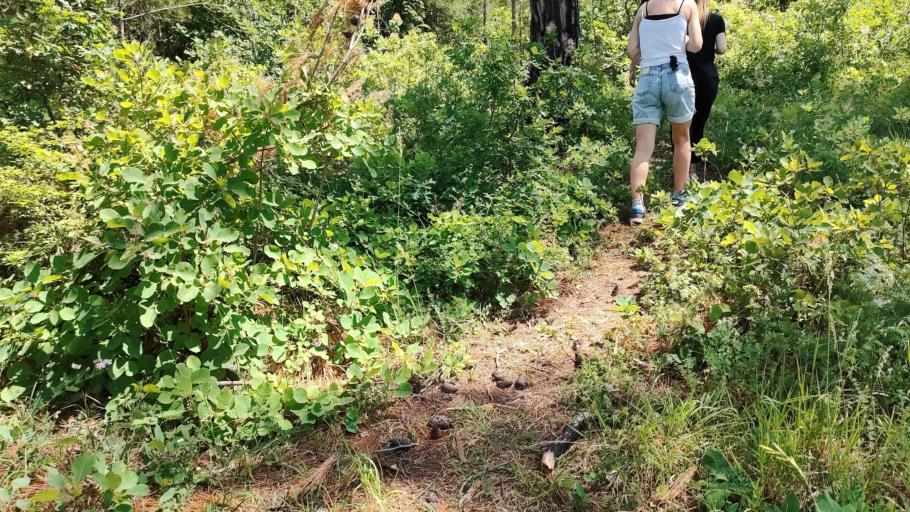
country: RU
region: Krasnodarskiy
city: Divnomorskoye
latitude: 44.4793
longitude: 38.1416
